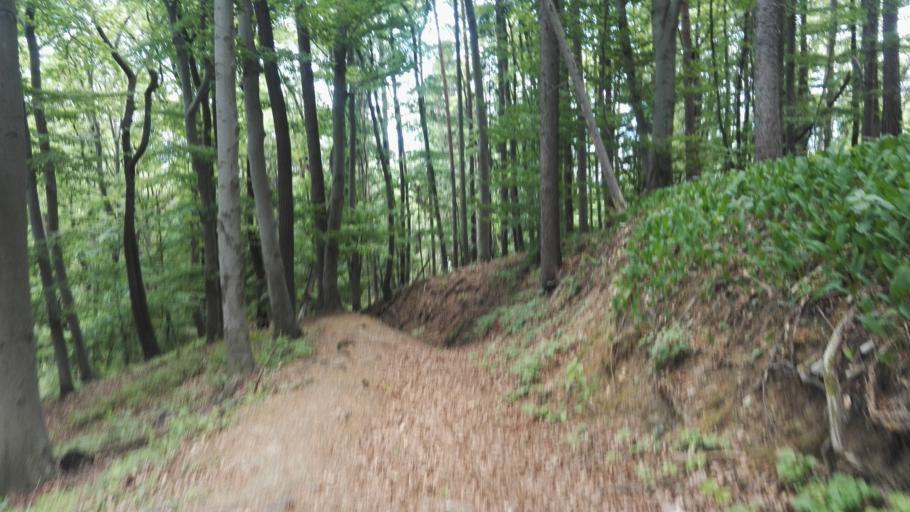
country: AT
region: Styria
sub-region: Graz Stadt
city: Goesting
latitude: 47.0872
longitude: 15.3902
